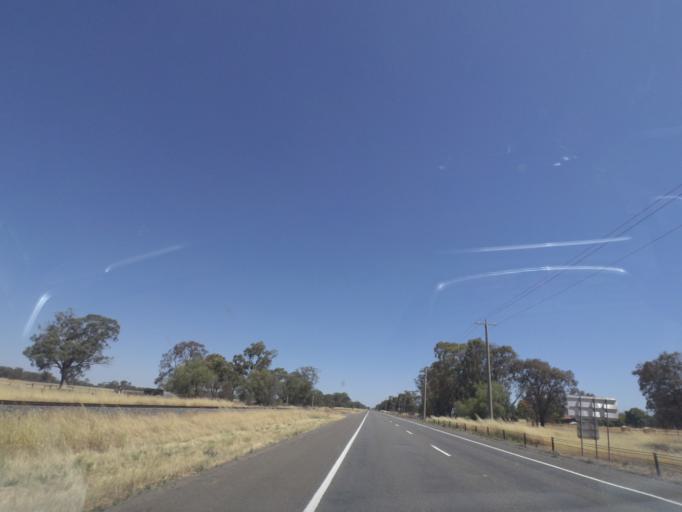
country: AU
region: Victoria
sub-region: Greater Shepparton
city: Shepparton
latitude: -36.2431
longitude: 145.4319
